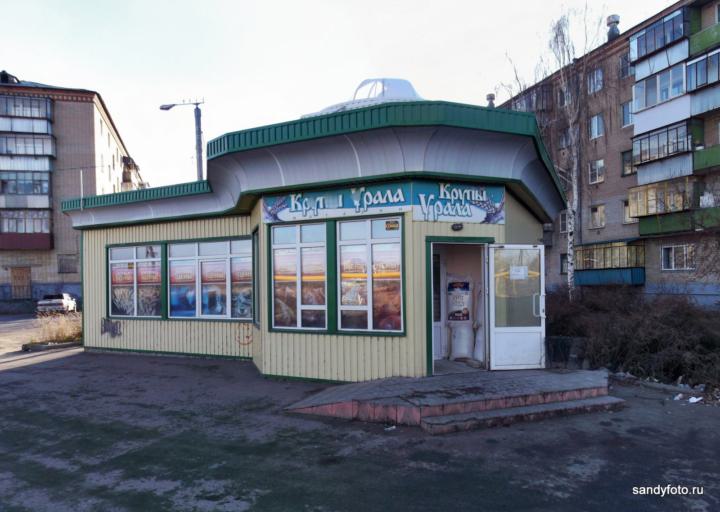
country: RU
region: Chelyabinsk
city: Troitsk
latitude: 54.0912
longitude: 61.5618
